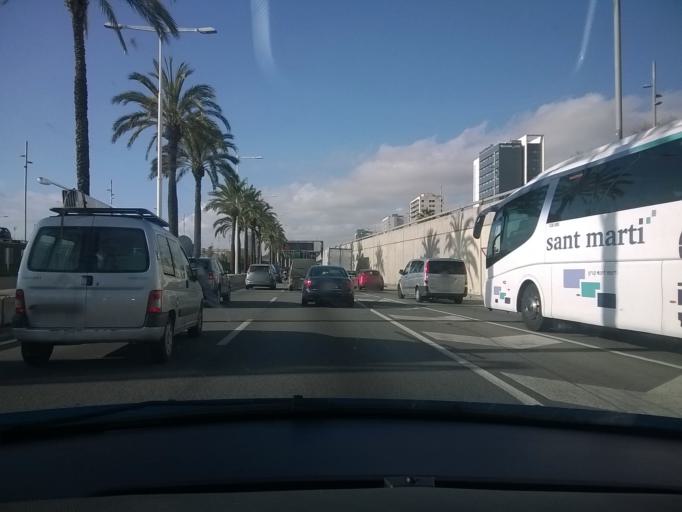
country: ES
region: Catalonia
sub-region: Provincia de Barcelona
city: Sant Marti
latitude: 41.4036
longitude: 2.2147
